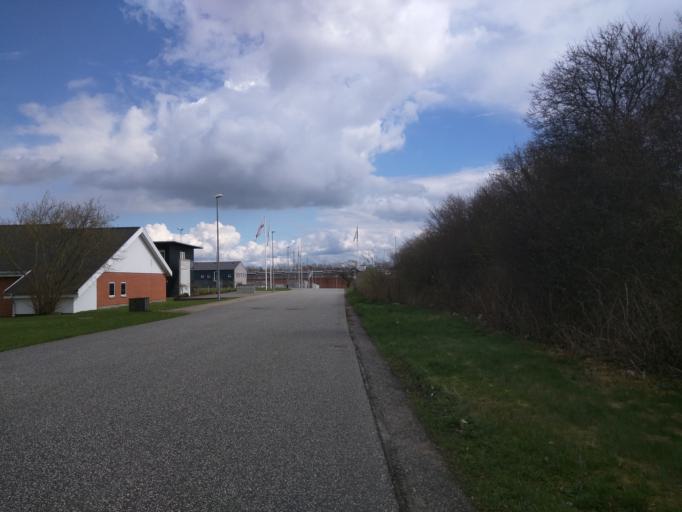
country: DK
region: South Denmark
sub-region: Fredericia Kommune
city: Snoghoj
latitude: 55.5434
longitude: 9.6992
